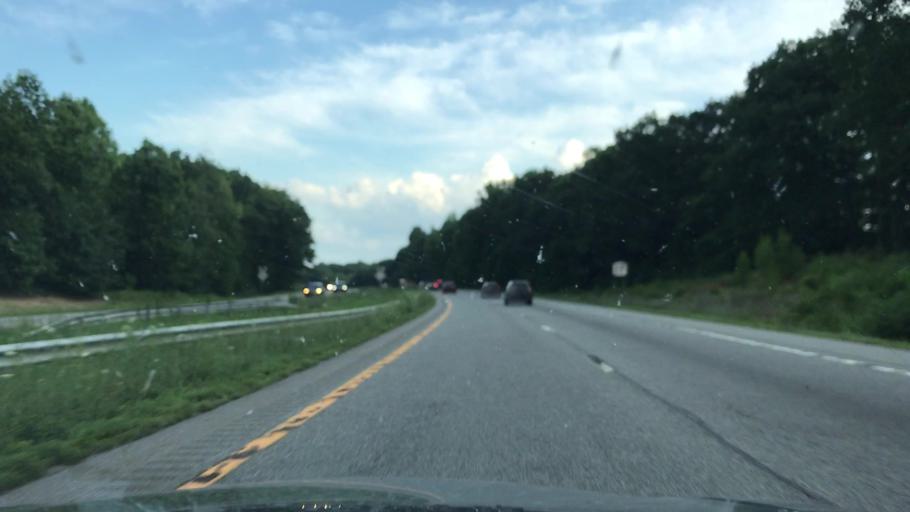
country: US
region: New York
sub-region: Sullivan County
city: Wurtsboro
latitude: 41.5460
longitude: -74.4258
